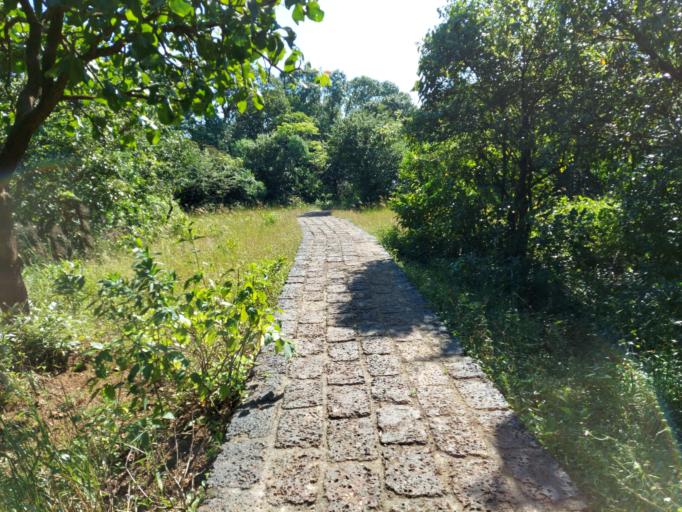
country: IN
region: Maharashtra
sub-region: Sindhudurg
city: Kudal
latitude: 16.0821
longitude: 73.8463
